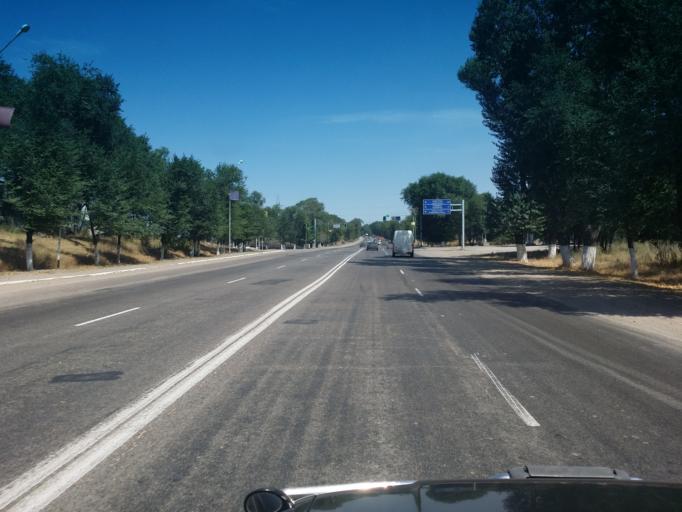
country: KZ
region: Almaty Oblysy
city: Talghar
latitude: 43.3992
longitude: 77.1684
